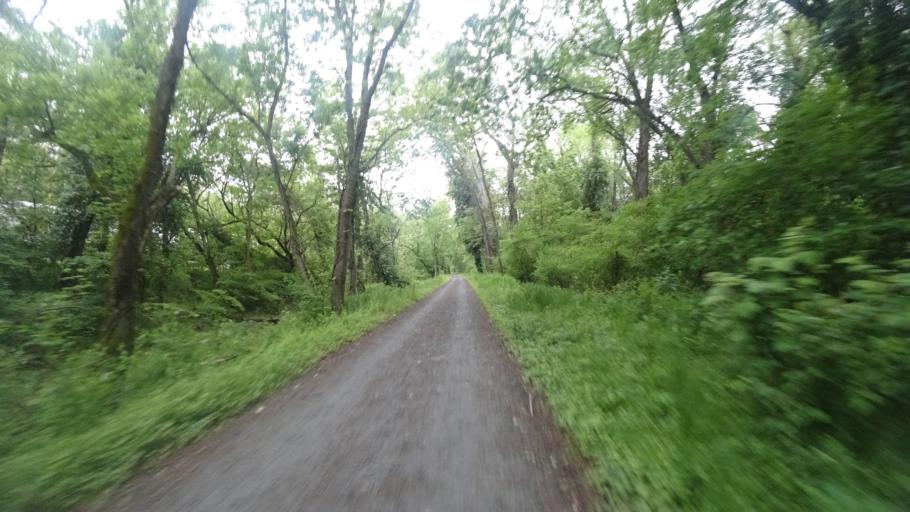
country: US
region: Maryland
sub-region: Frederick County
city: Brunswick
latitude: 39.3218
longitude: -77.6610
